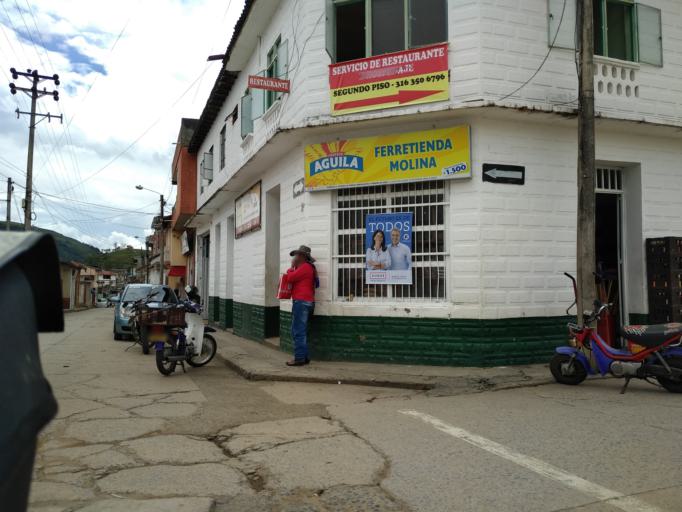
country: CO
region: Santander
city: Coromoro
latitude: 6.2849
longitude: -73.1462
